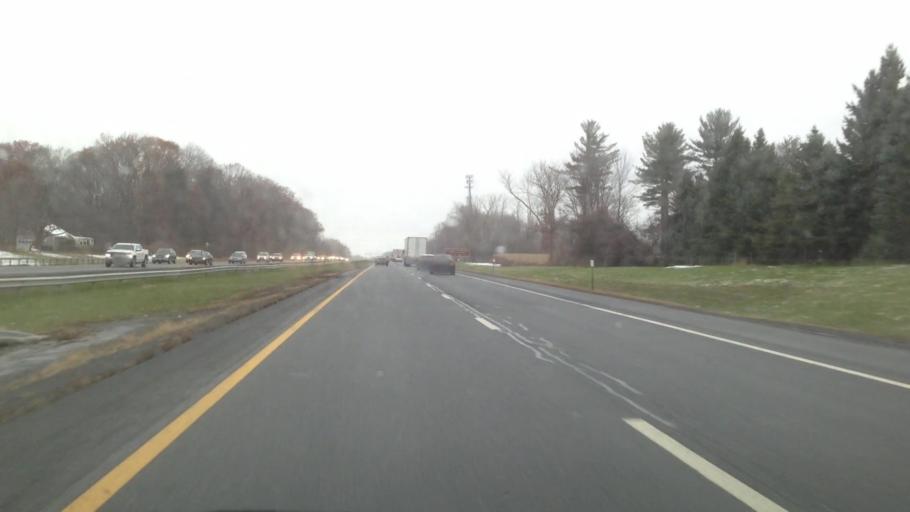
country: US
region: New York
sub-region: Albany County
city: Delmar
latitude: 42.5999
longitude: -73.7847
